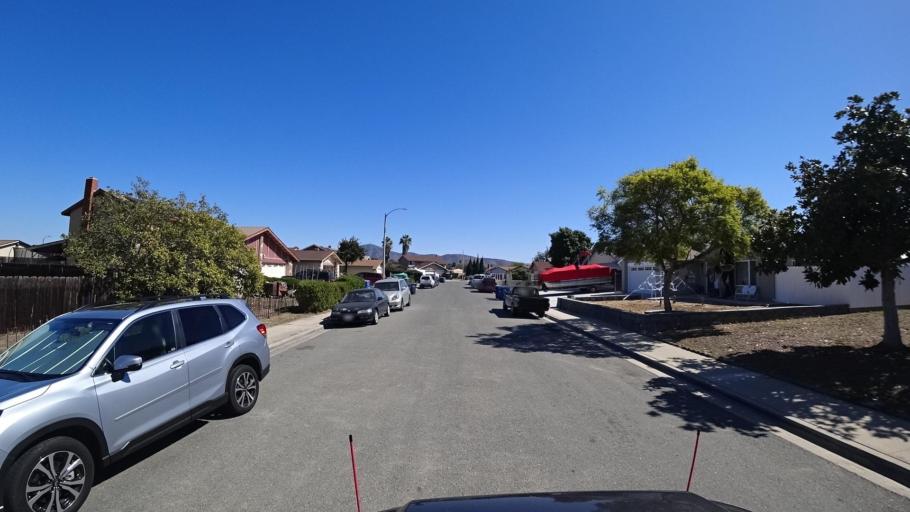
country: US
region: California
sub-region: San Diego County
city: La Presa
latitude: 32.6981
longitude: -117.0218
